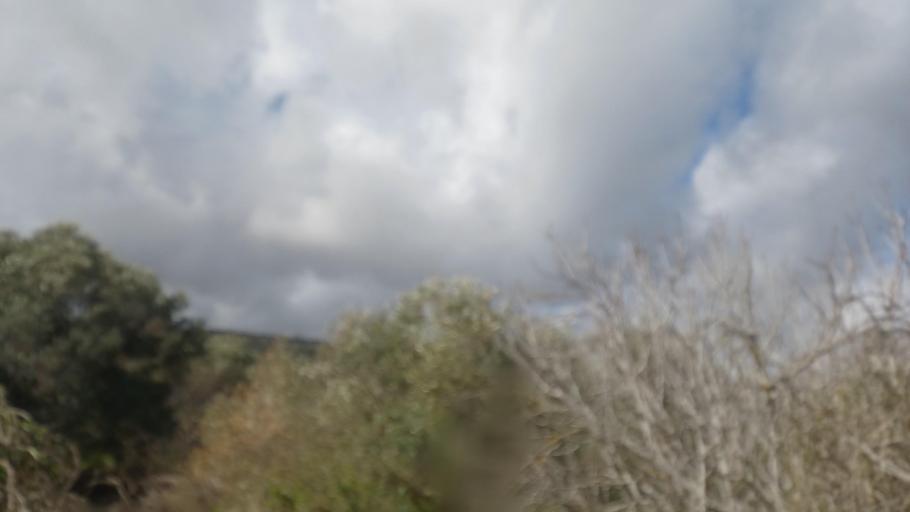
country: CY
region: Pafos
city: Polis
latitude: 34.9627
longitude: 32.4284
